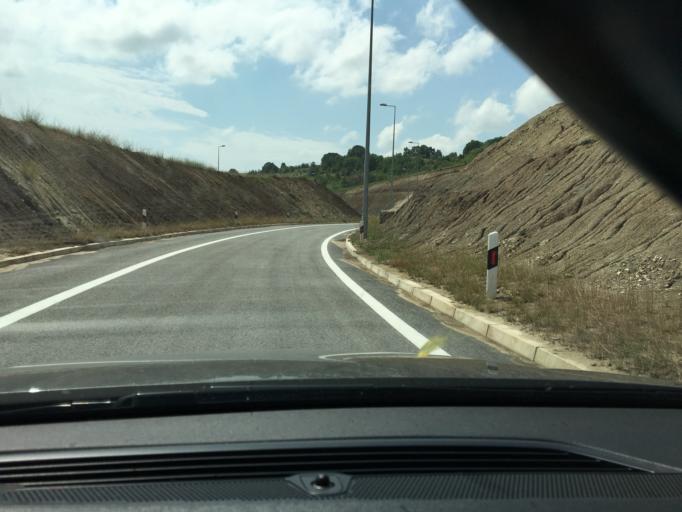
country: MK
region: Sveti Nikole
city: Gorobinci
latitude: 41.9173
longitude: 21.8765
